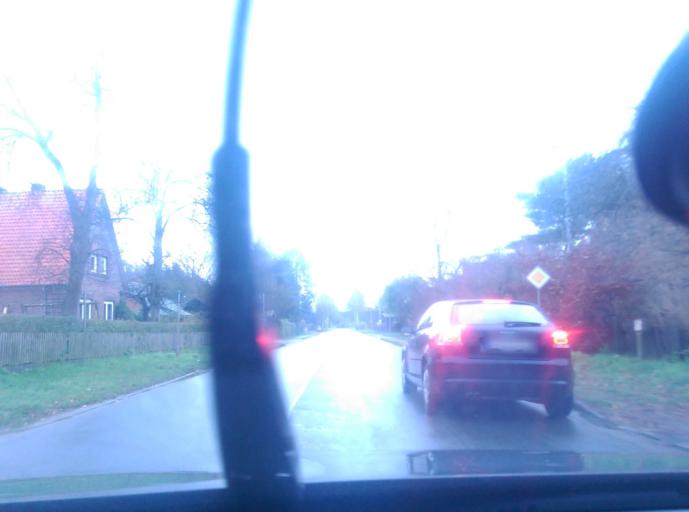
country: DE
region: Lower Saxony
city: Elze
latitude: 52.5743
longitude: 9.7148
